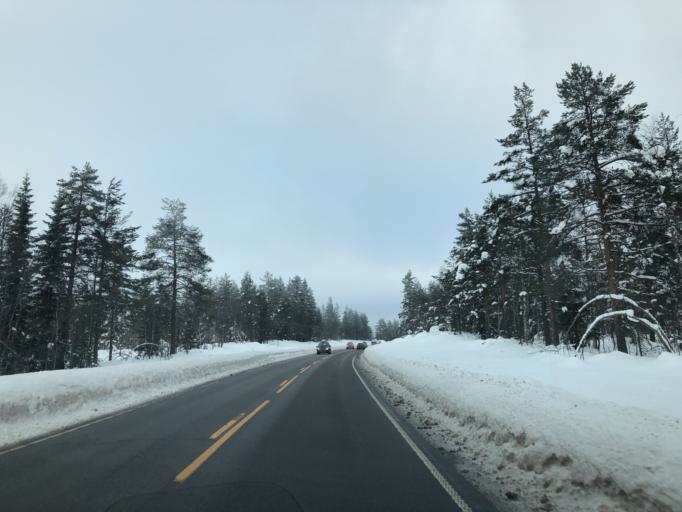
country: NO
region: Hedmark
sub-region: Trysil
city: Innbygda
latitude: 61.2325
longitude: 12.2548
